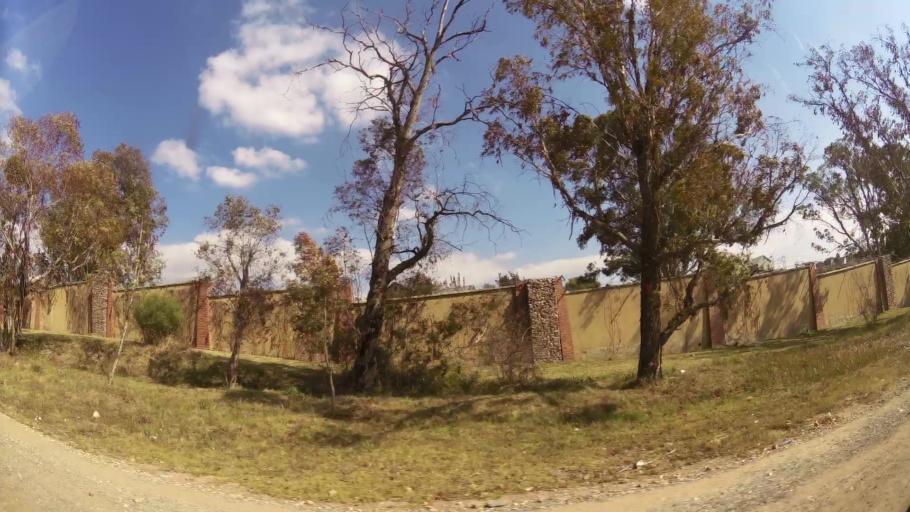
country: ZA
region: Gauteng
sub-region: City of Johannesburg Metropolitan Municipality
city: Midrand
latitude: -26.0144
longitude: 28.0831
